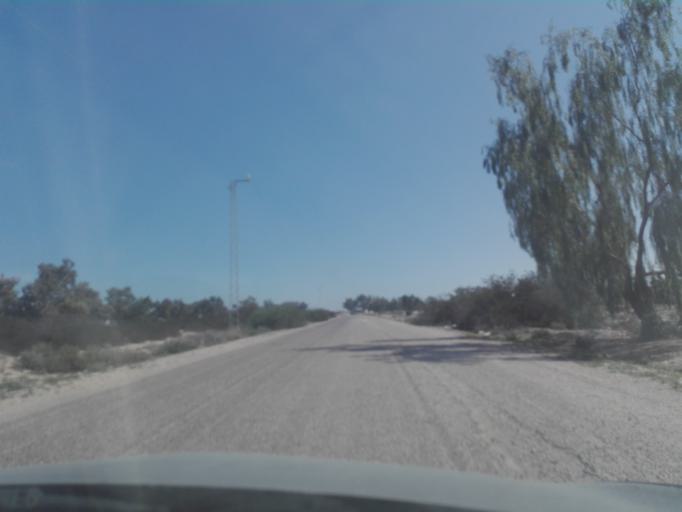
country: TN
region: Qabis
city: Gabes
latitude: 33.8721
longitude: 10.0354
